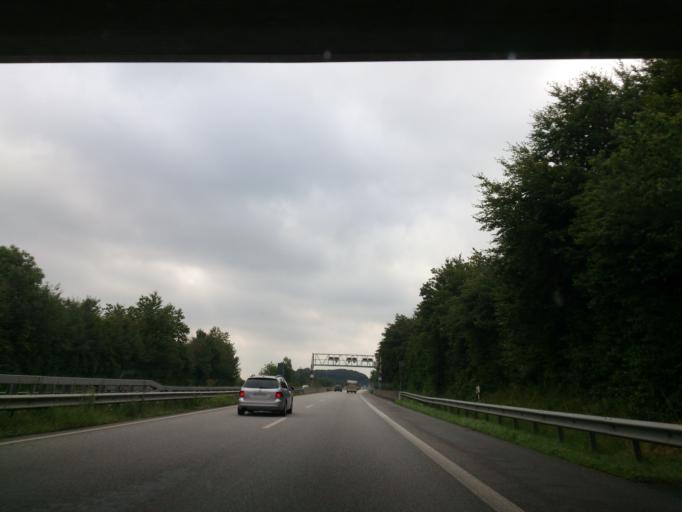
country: DE
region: Schleswig-Holstein
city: Kaisborstel
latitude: 54.0163
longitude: 9.4666
